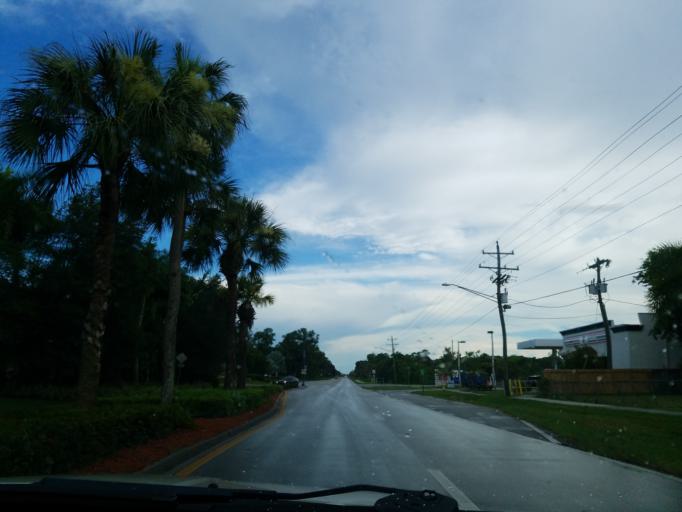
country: US
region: Florida
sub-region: Collier County
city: Immokalee
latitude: 26.4110
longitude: -81.4173
